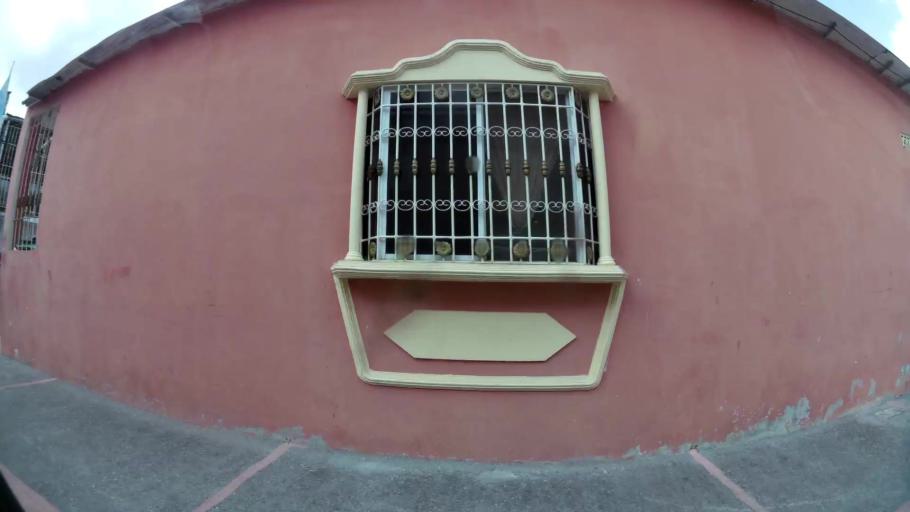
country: EC
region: Guayas
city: Guayaquil
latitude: -2.2314
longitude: -79.9066
